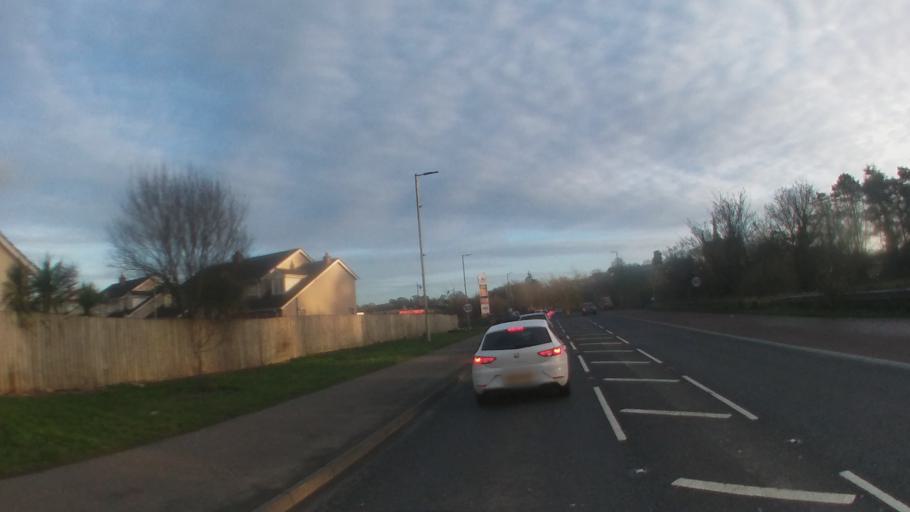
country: GB
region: Northern Ireland
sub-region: Armagh District
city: Armagh
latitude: 54.3569
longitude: -6.6633
